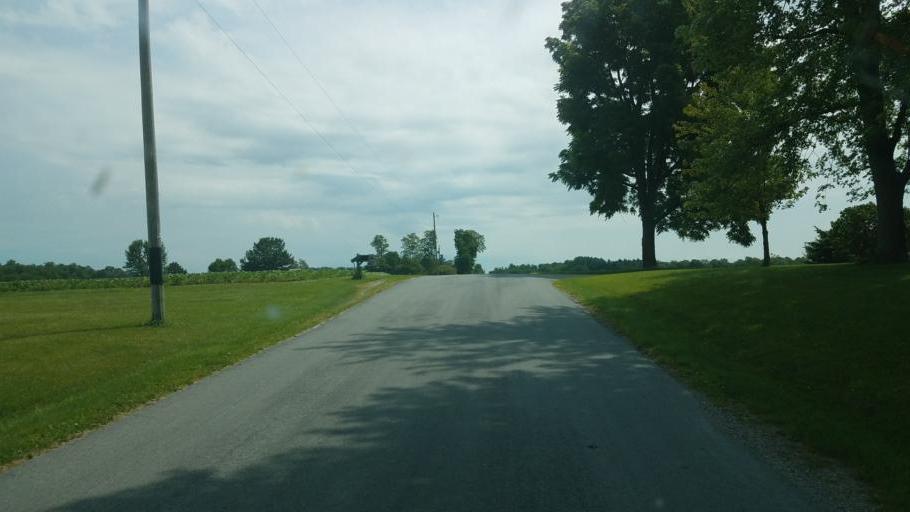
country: US
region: Ohio
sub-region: Wyandot County
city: Upper Sandusky
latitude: 40.8657
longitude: -83.2362
